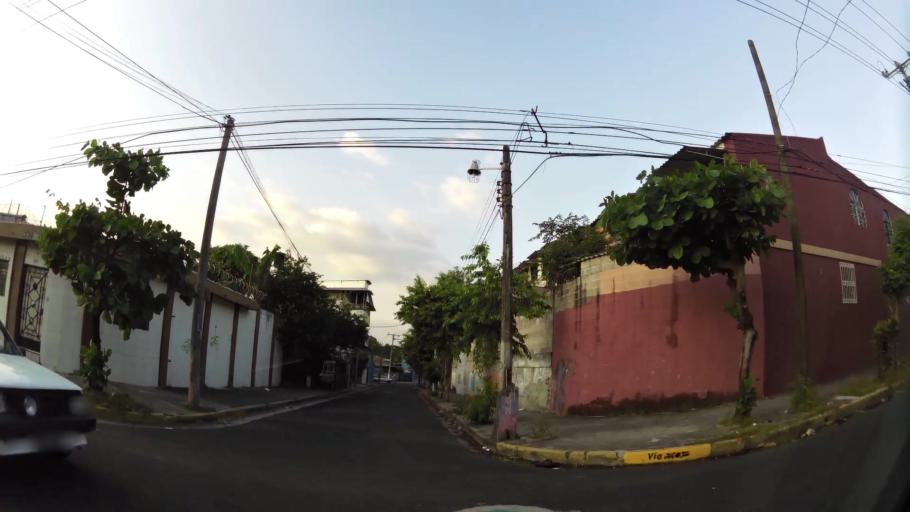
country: SV
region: San Salvador
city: Delgado
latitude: 13.7164
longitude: -89.1891
